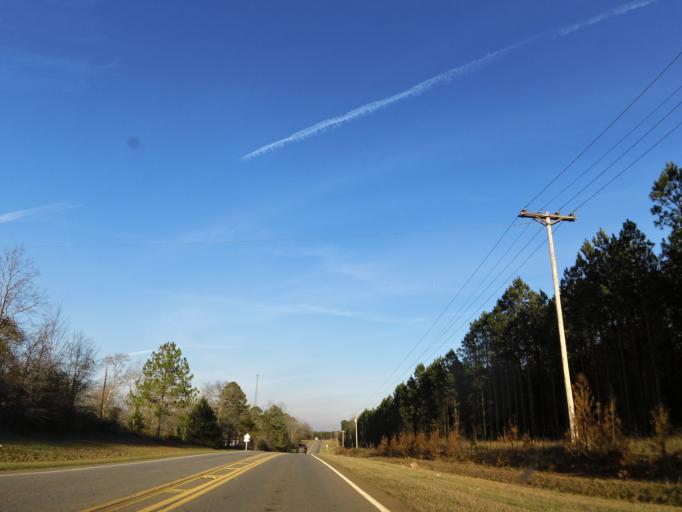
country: US
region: Georgia
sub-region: Sumter County
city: Americus
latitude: 32.0505
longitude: -84.3334
